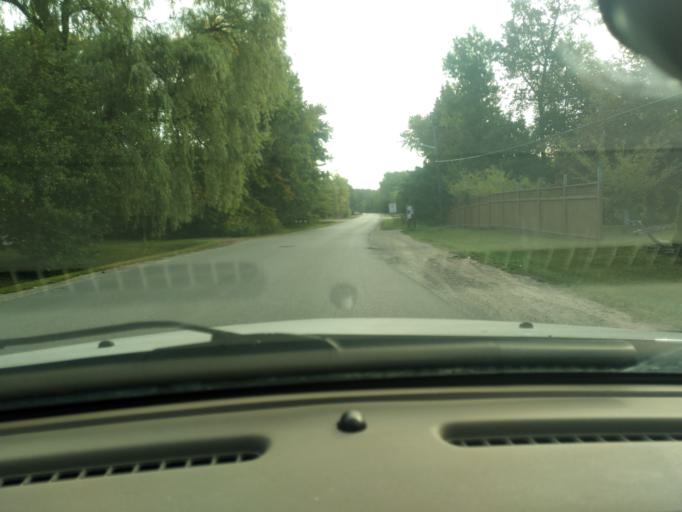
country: CA
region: Ontario
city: Innisfil
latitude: 44.3184
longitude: -79.5469
